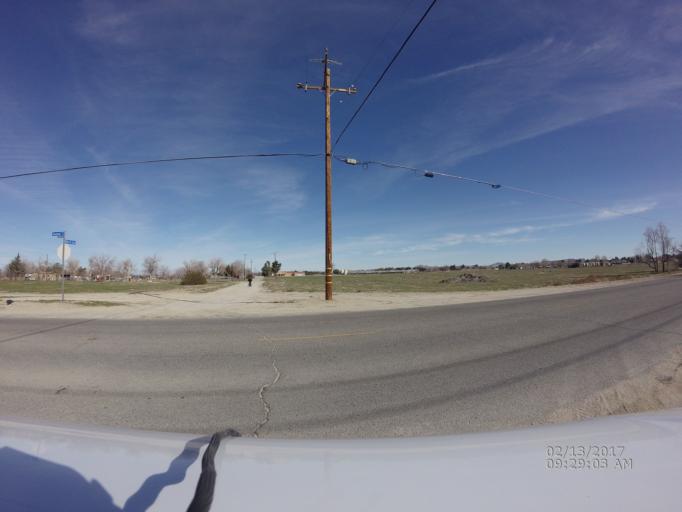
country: US
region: California
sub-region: Los Angeles County
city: Littlerock
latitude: 34.5429
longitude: -117.9625
